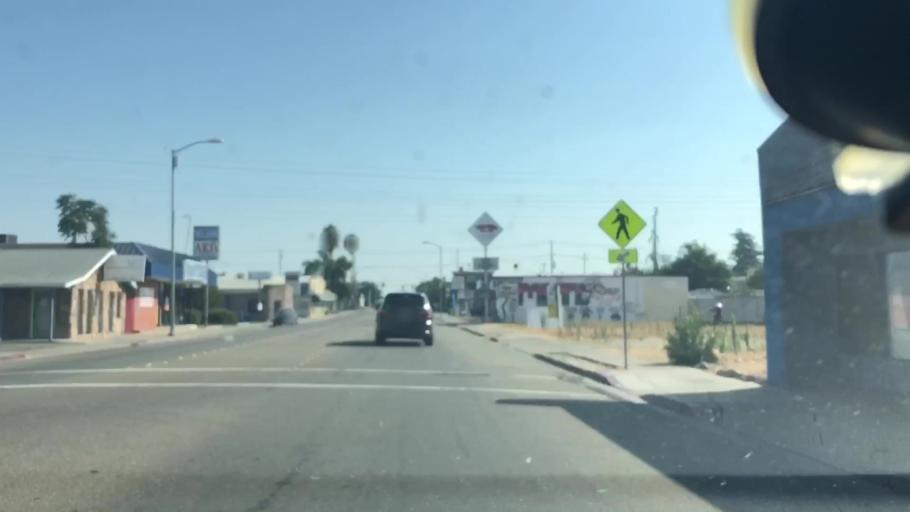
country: US
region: California
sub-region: San Joaquin County
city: Manteca
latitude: 37.8028
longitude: -121.2167
